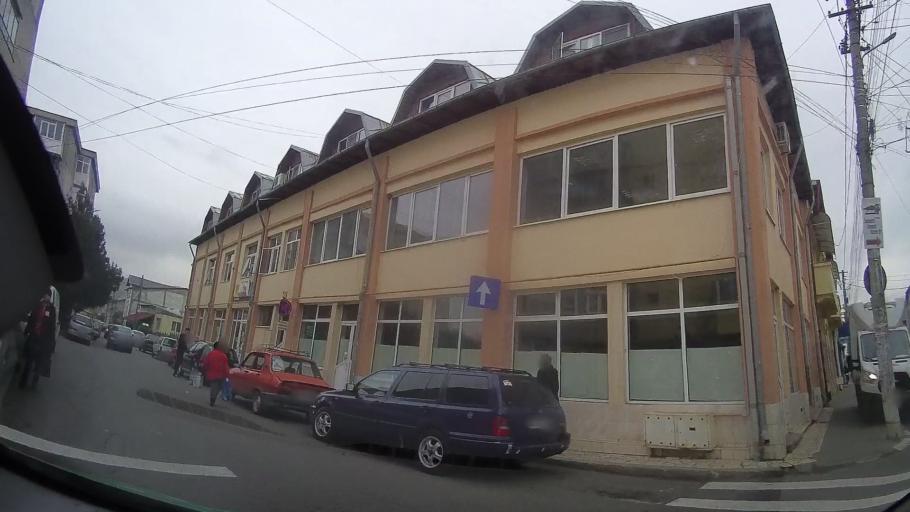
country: RO
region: Prahova
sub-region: Oras Urlati
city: Urlati
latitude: 44.9926
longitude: 26.2330
